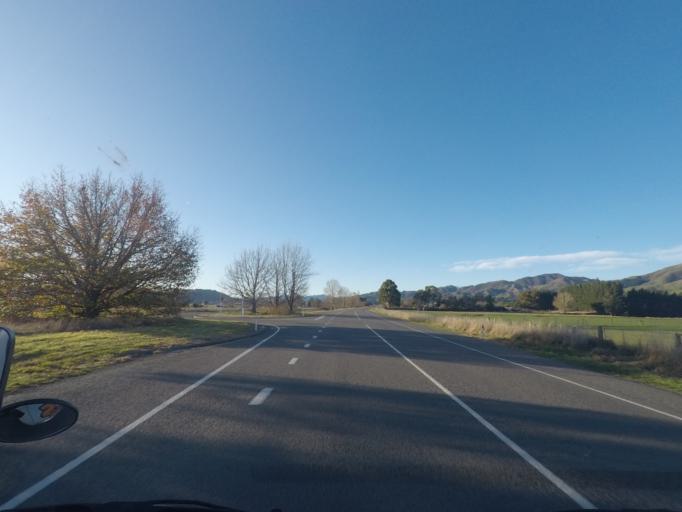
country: NZ
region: Canterbury
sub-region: Kaikoura District
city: Kaikoura
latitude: -42.7109
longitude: 173.2922
